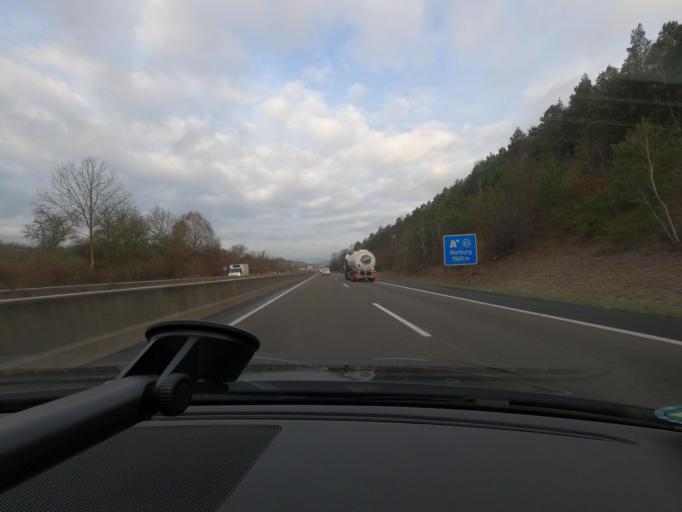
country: DE
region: North Rhine-Westphalia
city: Warburg
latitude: 51.4575
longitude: 9.1253
